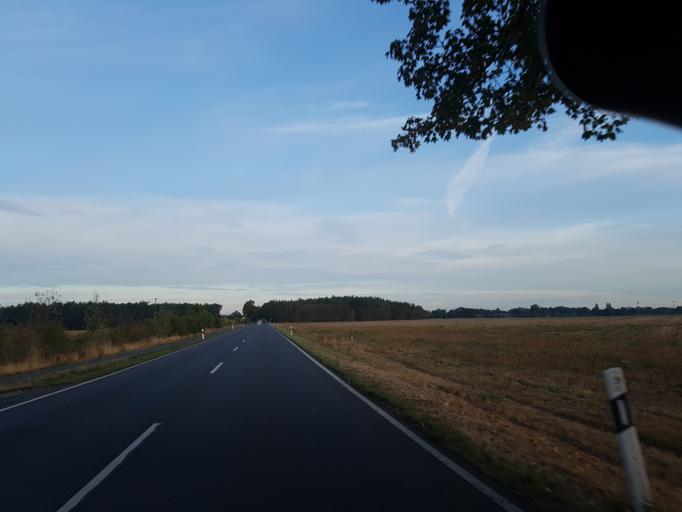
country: DE
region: Brandenburg
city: Sonnewalde
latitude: 51.6599
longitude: 13.6551
